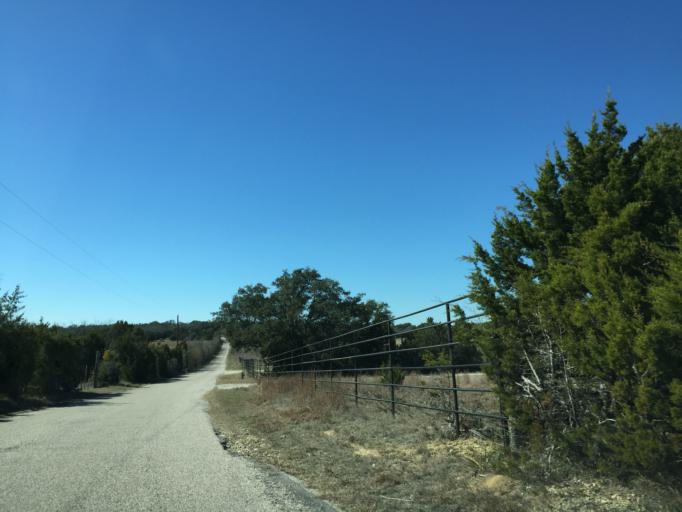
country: US
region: Texas
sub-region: Lampasas County
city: Kempner
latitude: 30.9320
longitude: -98.0367
